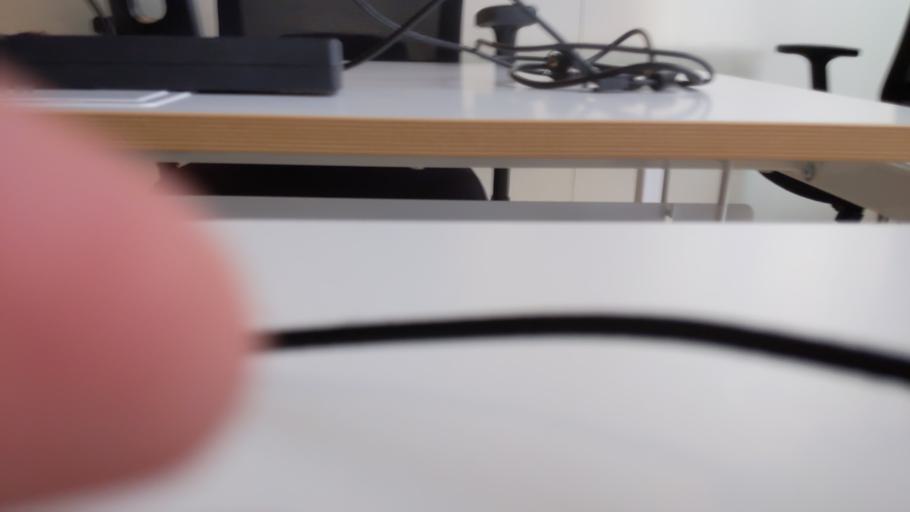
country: RU
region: Moskovskaya
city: Rogachevo
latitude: 56.4246
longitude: 37.1019
